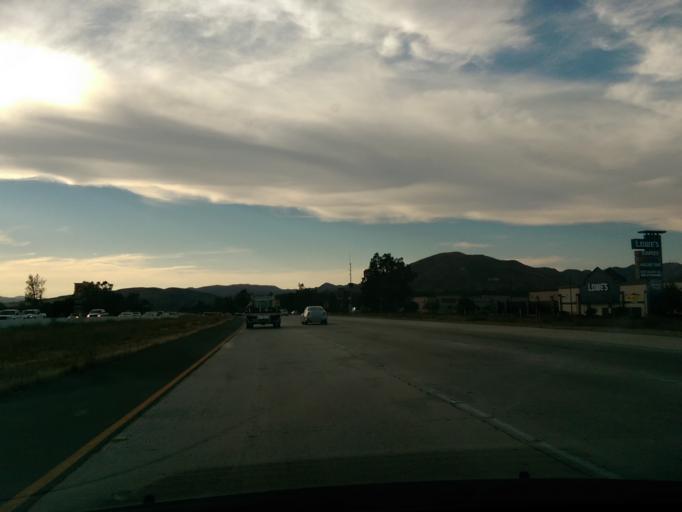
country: US
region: California
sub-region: Riverside County
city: Lake Elsinore
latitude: 33.6925
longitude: -117.3379
